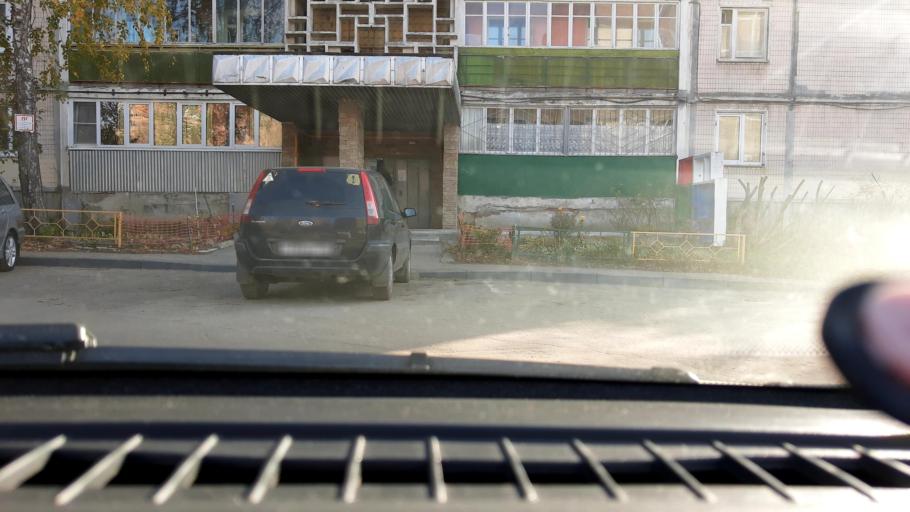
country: RU
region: Nizjnij Novgorod
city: Gorbatovka
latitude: 56.3597
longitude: 43.8192
